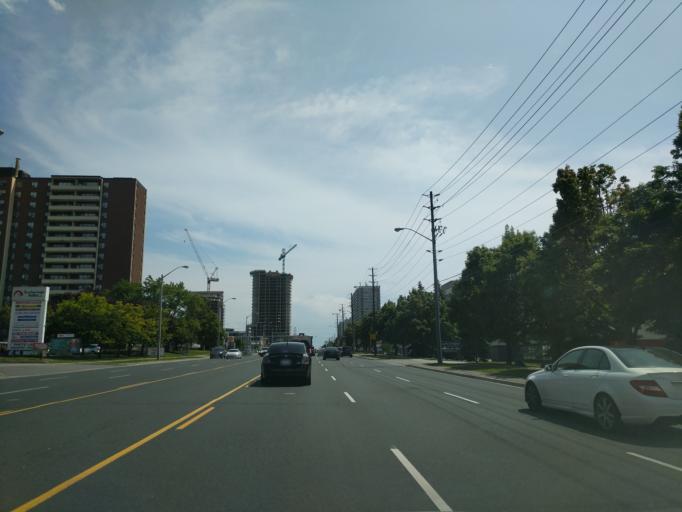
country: CA
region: Ontario
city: Scarborough
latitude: 43.7787
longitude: -79.2327
